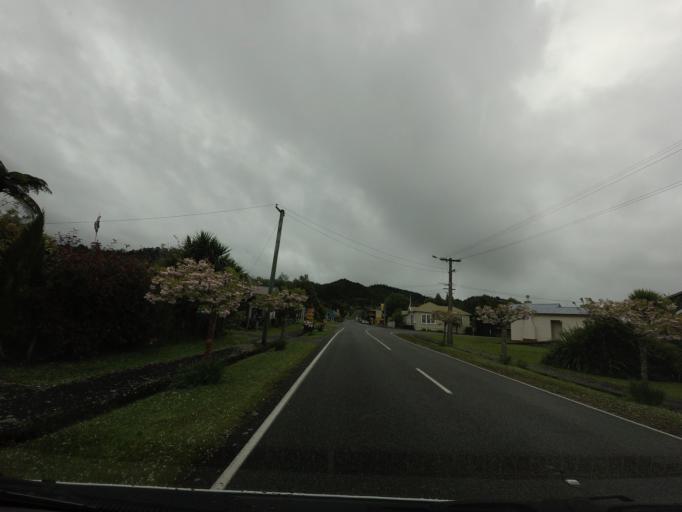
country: NZ
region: West Coast
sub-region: Westland District
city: Hokitika
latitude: -42.8991
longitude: 170.8180
